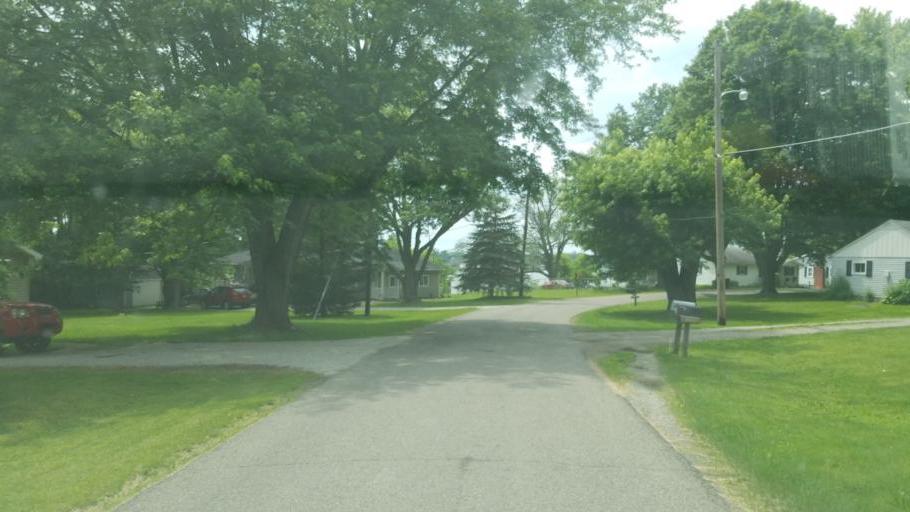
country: US
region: Ohio
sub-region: Perry County
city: Thornport
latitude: 39.9225
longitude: -82.4113
